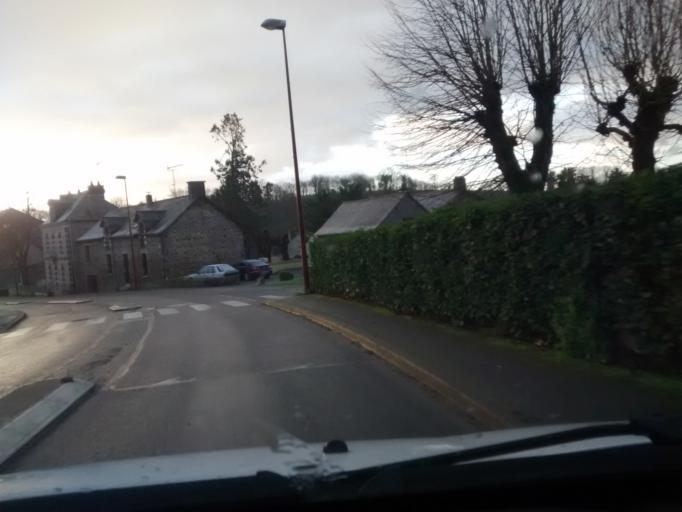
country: FR
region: Brittany
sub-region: Departement d'Ille-et-Vilaine
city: Domalain
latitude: 47.9651
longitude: -1.2649
